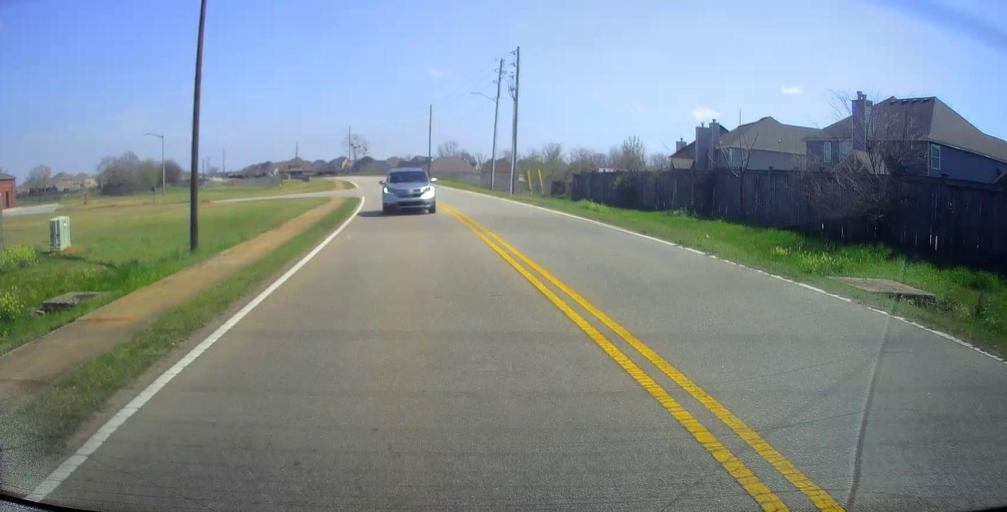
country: US
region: Georgia
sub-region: Houston County
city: Centerville
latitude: 32.5672
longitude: -83.7121
